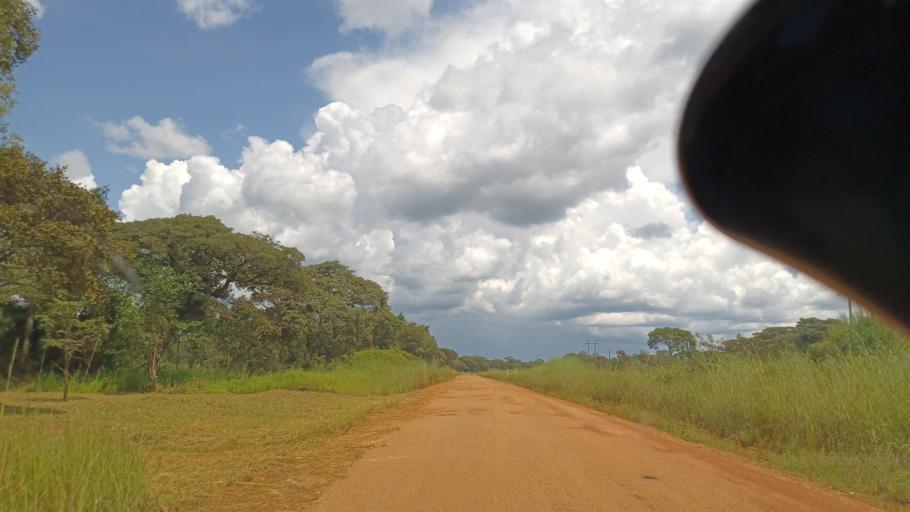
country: ZM
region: North-Western
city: Solwezi
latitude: -12.6909
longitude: 26.0403
